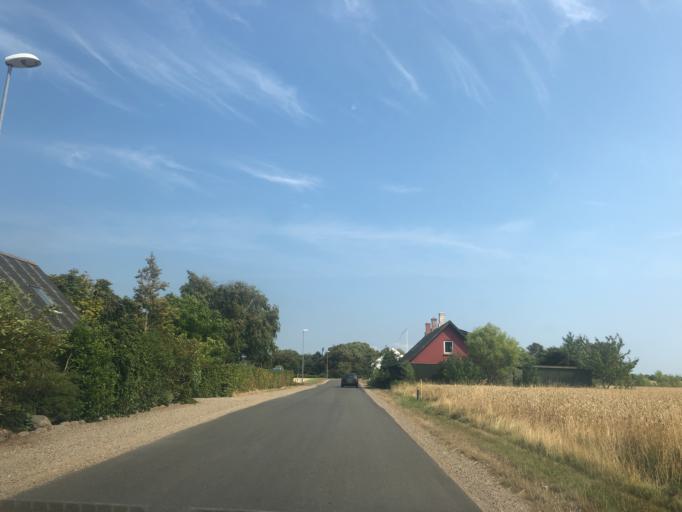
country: DK
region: North Denmark
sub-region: Morso Kommune
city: Nykobing Mors
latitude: 56.8208
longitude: 9.0011
